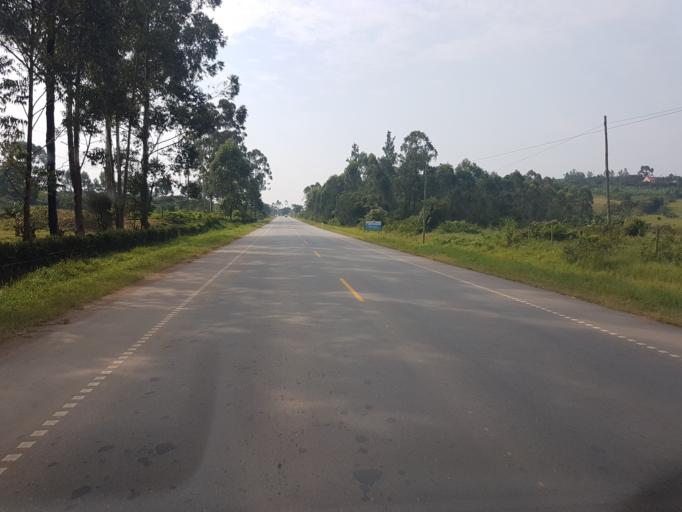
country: UG
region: Western Region
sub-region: Mbarara District
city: Bwizibwera
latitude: -0.6411
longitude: 30.5557
